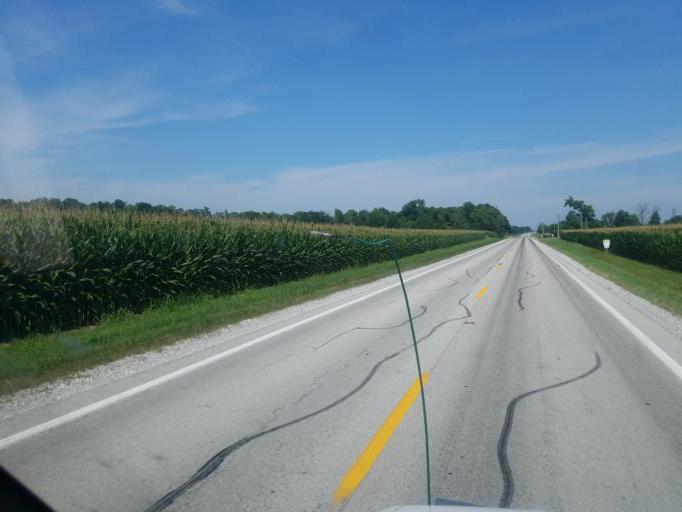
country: US
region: Ohio
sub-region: Shelby County
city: Botkins
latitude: 40.4962
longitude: -84.2843
